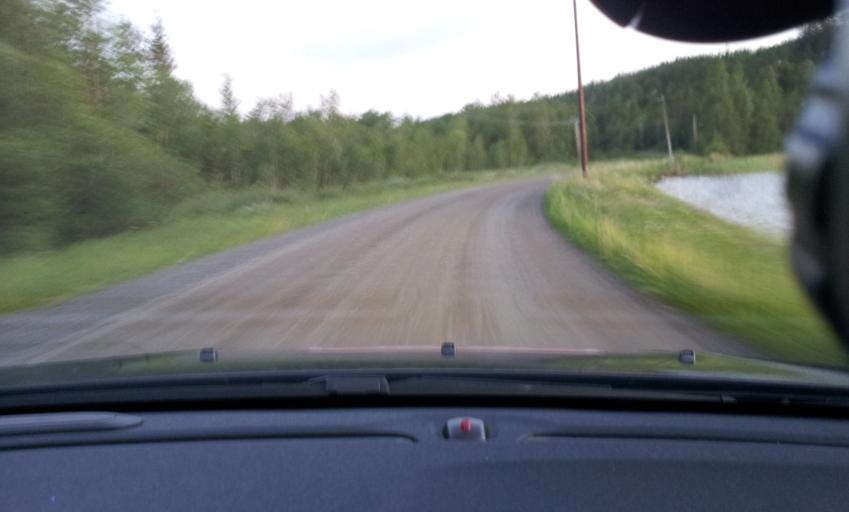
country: SE
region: Jaemtland
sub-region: Ragunda Kommun
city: Hammarstrand
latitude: 62.9527
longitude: 16.1142
